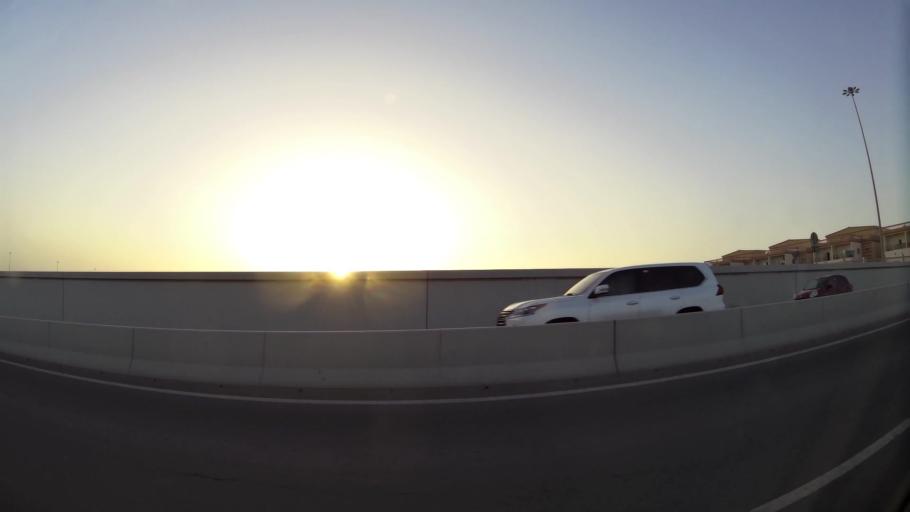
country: QA
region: Baladiyat ar Rayyan
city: Ar Rayyan
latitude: 25.3226
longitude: 51.4606
